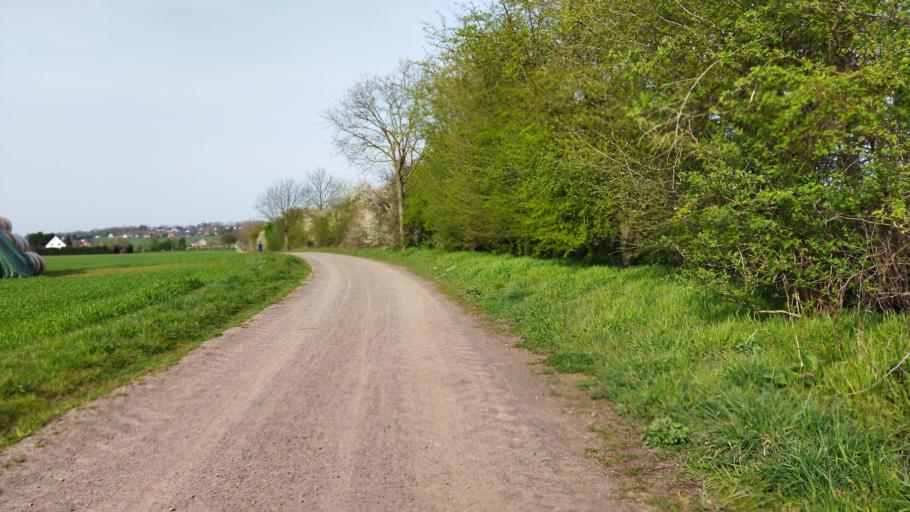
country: DE
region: Lower Saxony
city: Buckeburg
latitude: 52.2009
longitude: 8.9940
